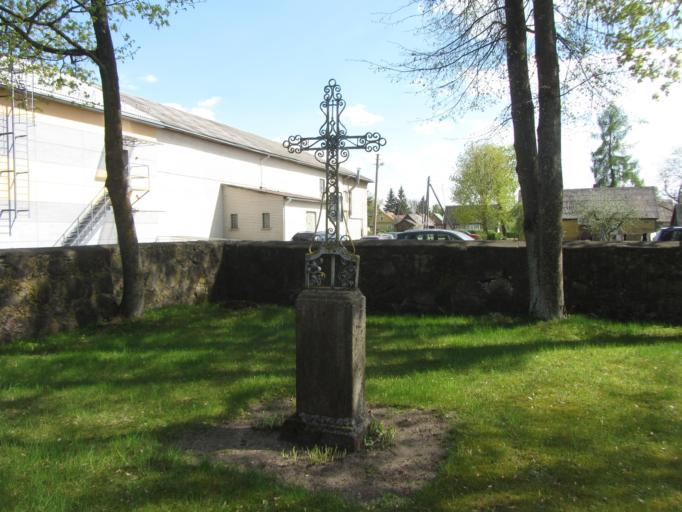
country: LT
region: Utenos apskritis
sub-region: Anyksciai
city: Anyksciai
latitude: 55.4144
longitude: 25.0618
